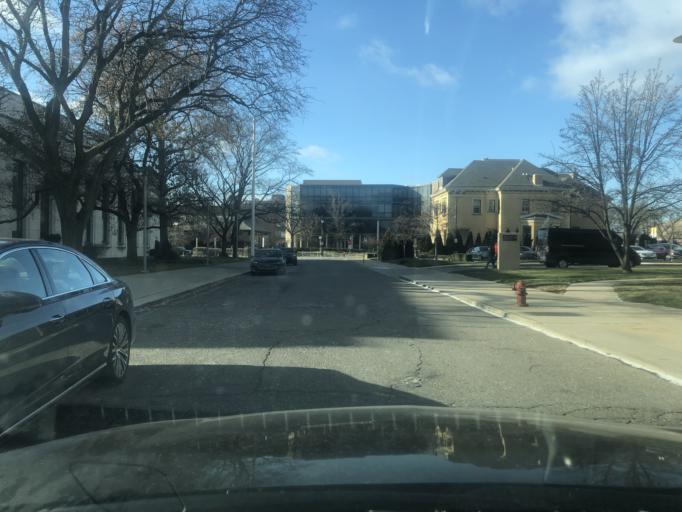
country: US
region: Michigan
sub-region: Wayne County
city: Detroit
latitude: 42.3594
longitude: -83.0672
